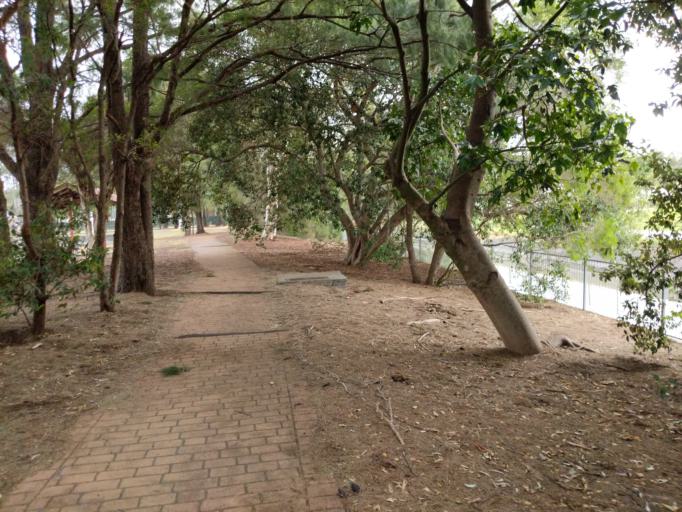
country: AU
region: New South Wales
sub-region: Ashfield
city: Croydon
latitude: -33.8654
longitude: 151.1119
